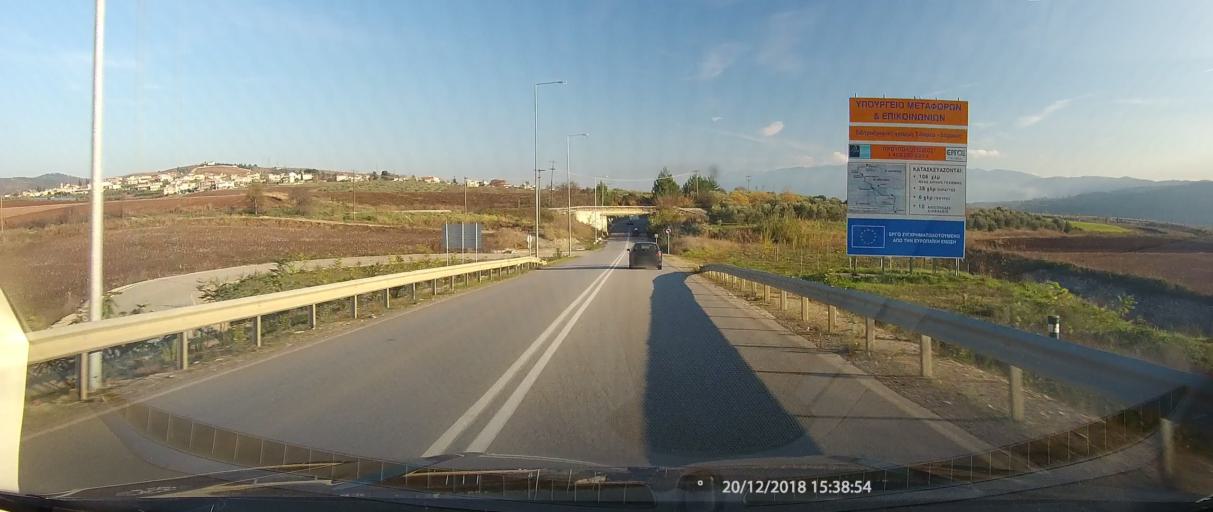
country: GR
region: Central Greece
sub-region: Nomos Fthiotidos
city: Stavros
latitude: 38.9004
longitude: 22.3575
